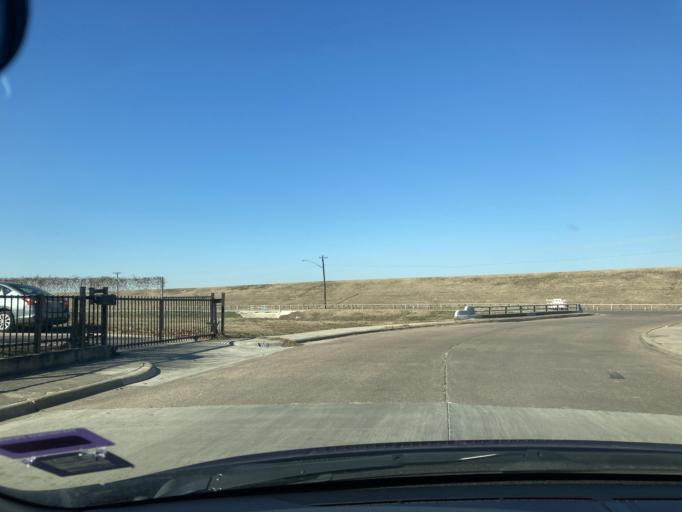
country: US
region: Texas
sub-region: Dallas County
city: Dallas
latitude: 32.7870
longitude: -96.8398
